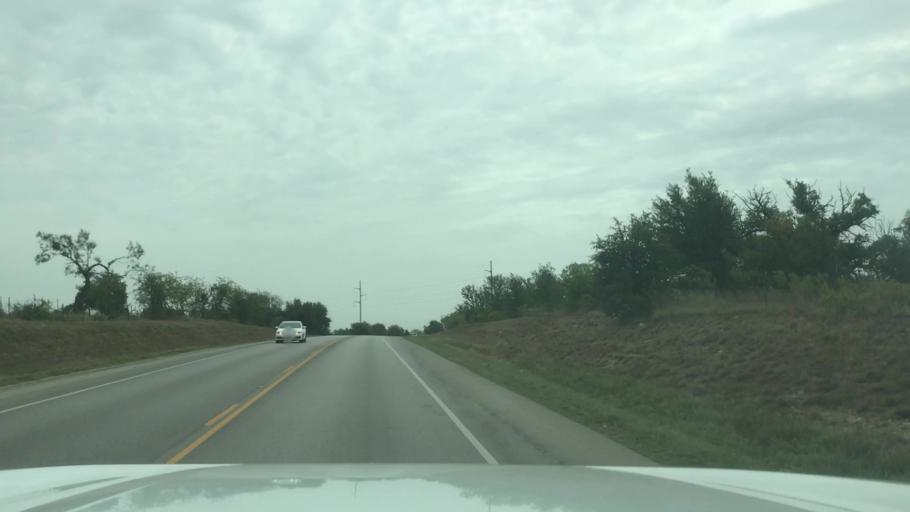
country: US
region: Texas
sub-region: Erath County
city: Dublin
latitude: 32.0976
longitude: -98.3842
